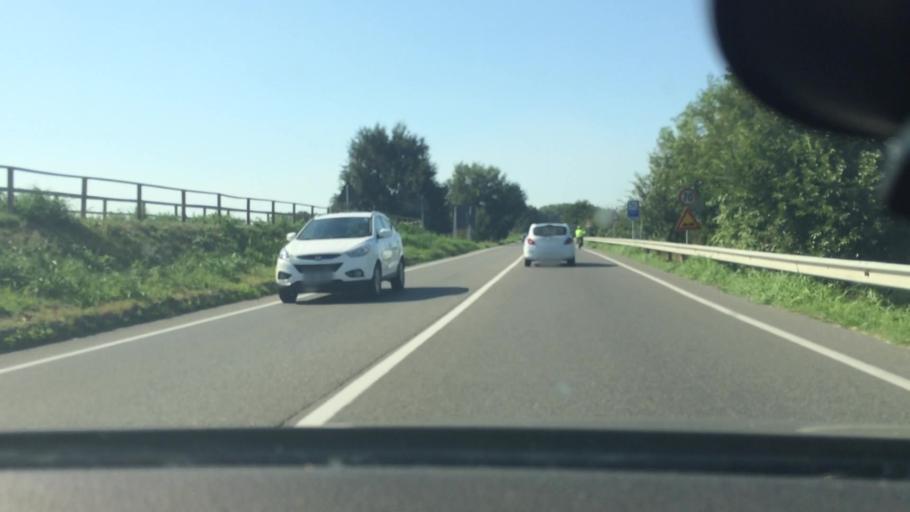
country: IT
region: Lombardy
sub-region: Provincia di Lodi
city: San Rocco al Porto
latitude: 45.0842
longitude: 9.6909
